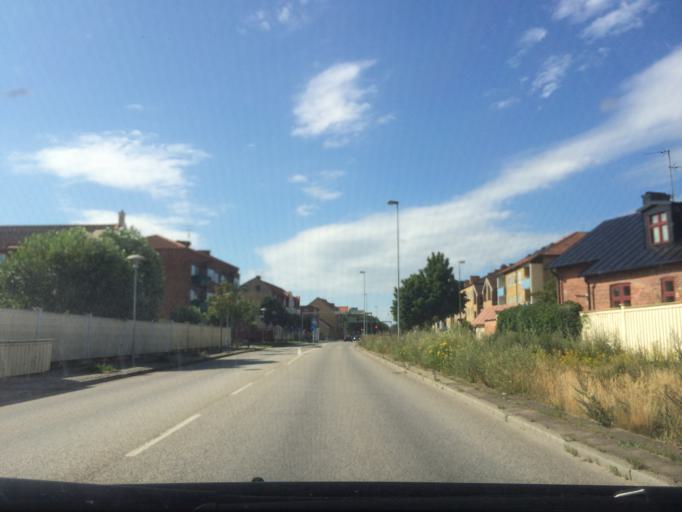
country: SE
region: Skane
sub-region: Malmo
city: Bunkeflostrand
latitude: 55.5837
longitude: 12.9302
